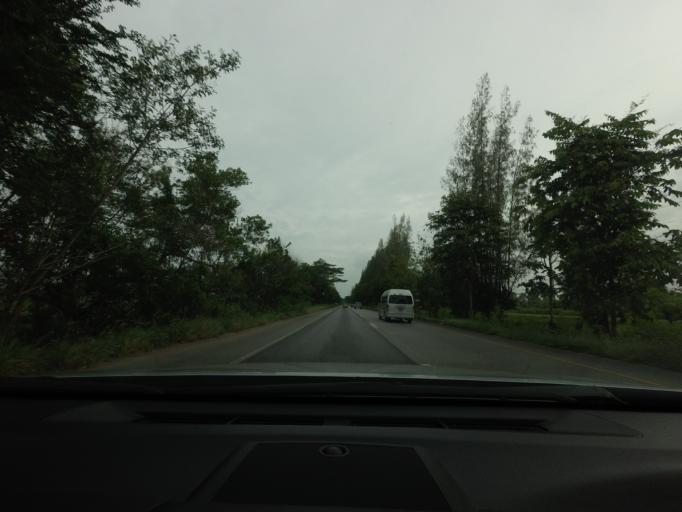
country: TH
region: Prachuap Khiri Khan
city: Hua Hin
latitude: 12.6597
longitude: 99.8751
